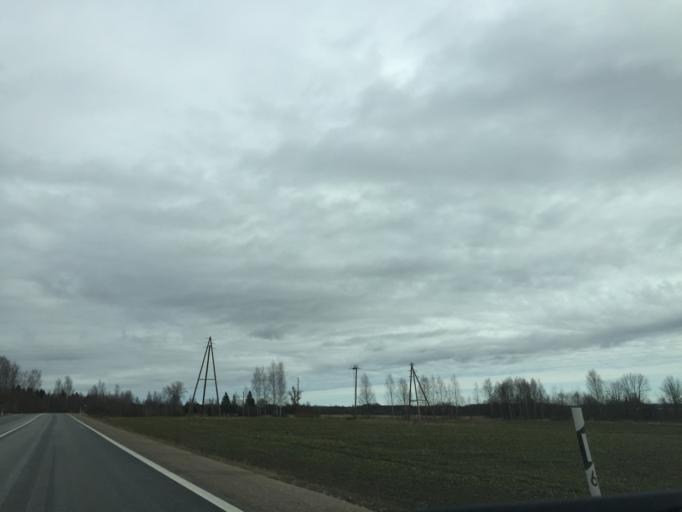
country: LV
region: Daugavpils
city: Daugavpils
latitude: 55.9244
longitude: 26.6823
